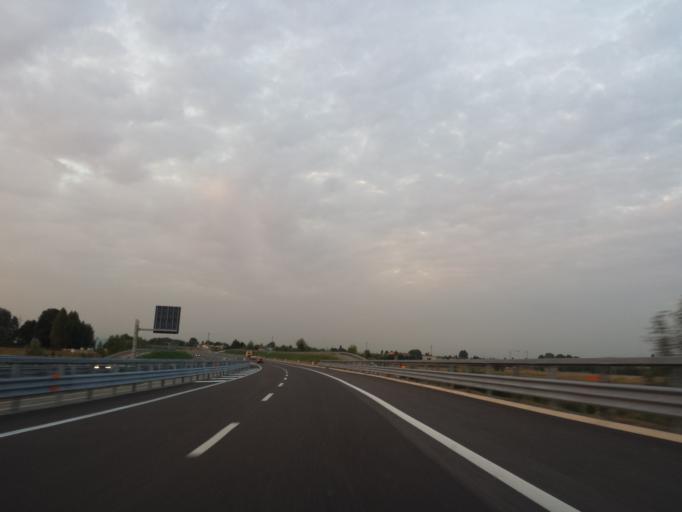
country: IT
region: Veneto
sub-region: Provincia di Vicenza
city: Longare
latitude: 45.4665
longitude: 11.6349
